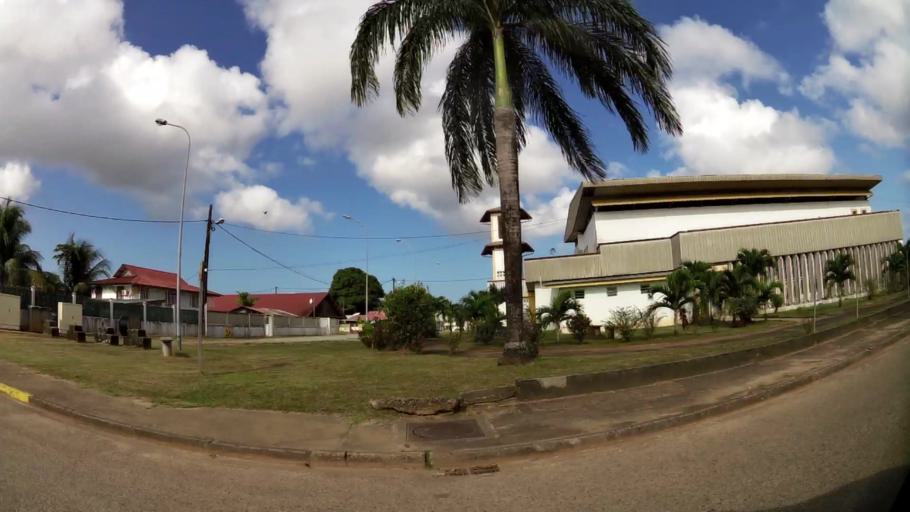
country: GF
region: Guyane
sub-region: Guyane
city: Cayenne
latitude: 4.9340
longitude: -52.3248
